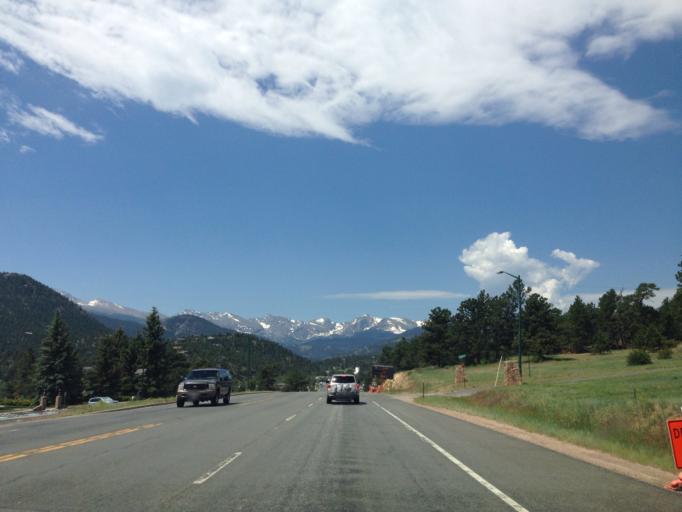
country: US
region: Colorado
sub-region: Larimer County
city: Estes Park
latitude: 40.3828
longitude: -105.5076
